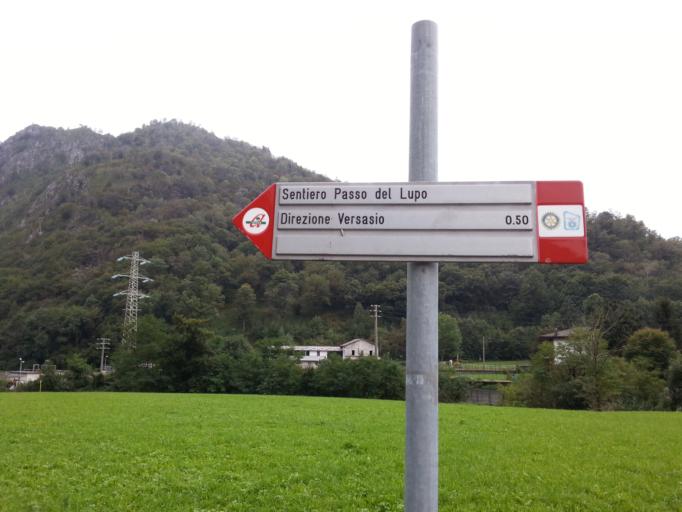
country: IT
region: Lombardy
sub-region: Provincia di Lecco
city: Ballabio
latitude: 45.8870
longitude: 9.4262
